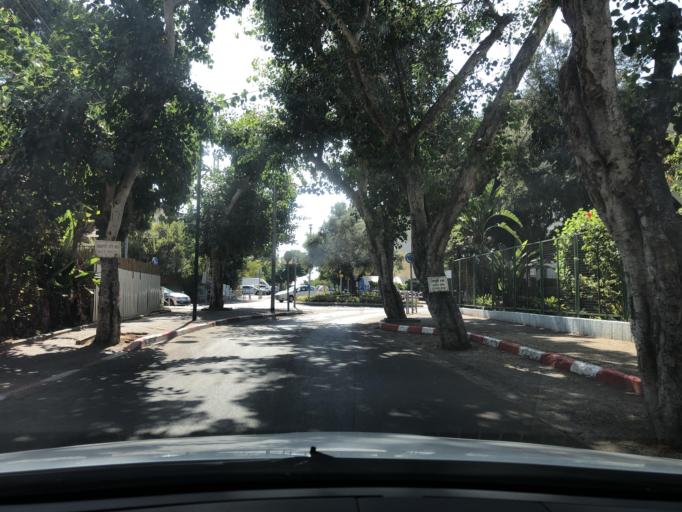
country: IL
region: Central District
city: Kfar Saba
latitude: 32.1761
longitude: 34.8971
